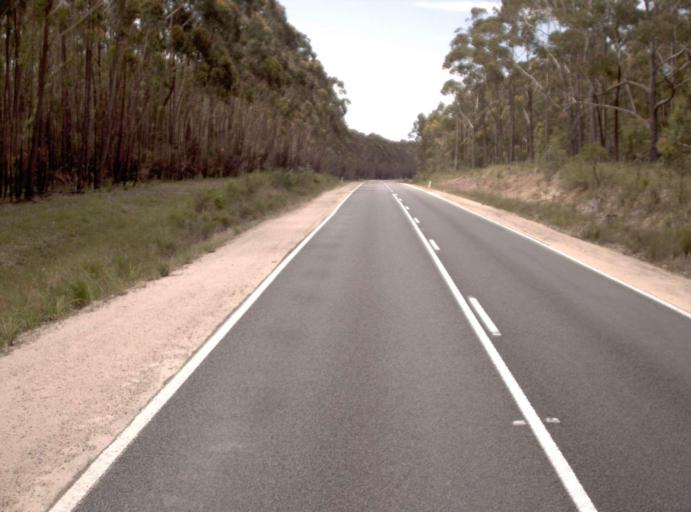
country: AU
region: New South Wales
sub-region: Bega Valley
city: Eden
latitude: -37.5291
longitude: 149.4877
